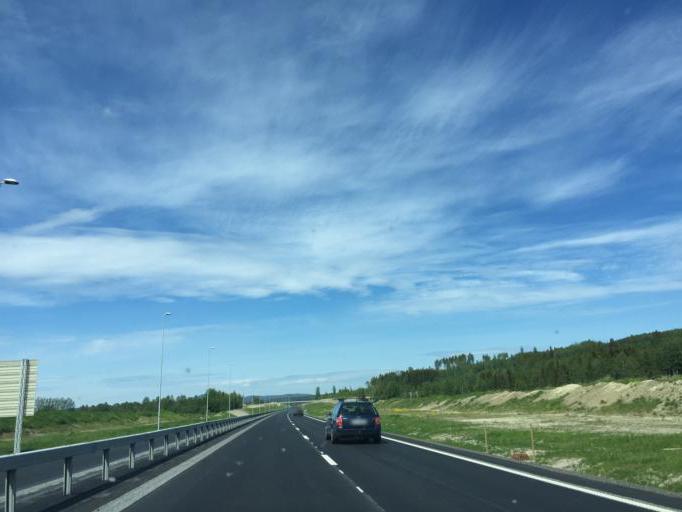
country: NO
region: Hedmark
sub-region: Kongsvinger
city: Spetalen
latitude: 60.2377
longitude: 11.8056
